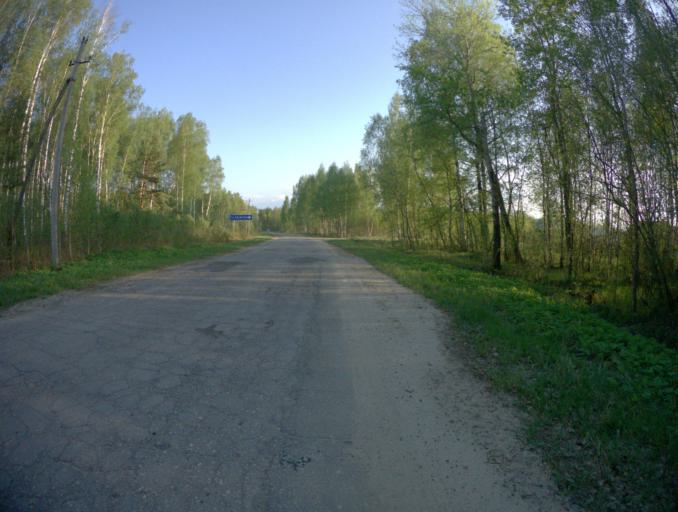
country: RU
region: Vladimir
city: Vyazniki
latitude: 56.3302
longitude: 42.1235
